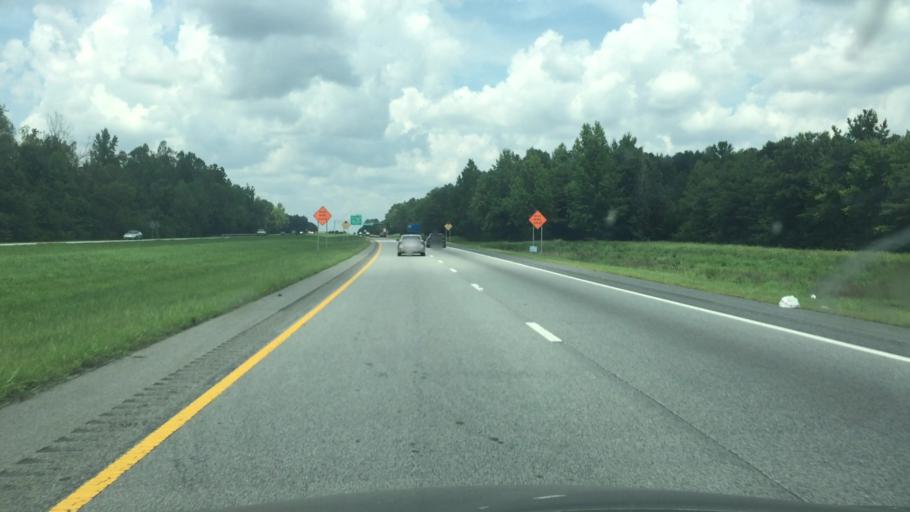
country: US
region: North Carolina
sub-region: Guilford County
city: Pleasant Garden
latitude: 35.9778
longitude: -79.8219
